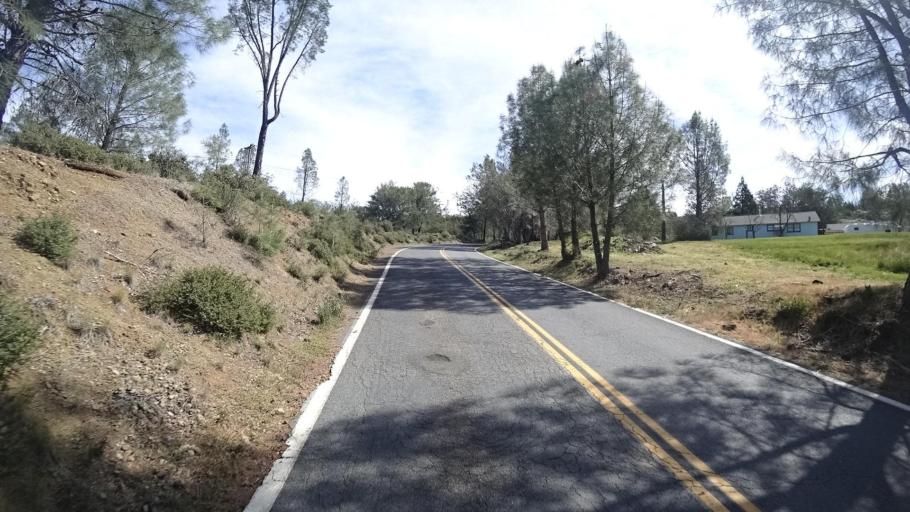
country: US
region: California
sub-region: Lake County
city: Cobb
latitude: 38.8572
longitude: -122.7583
